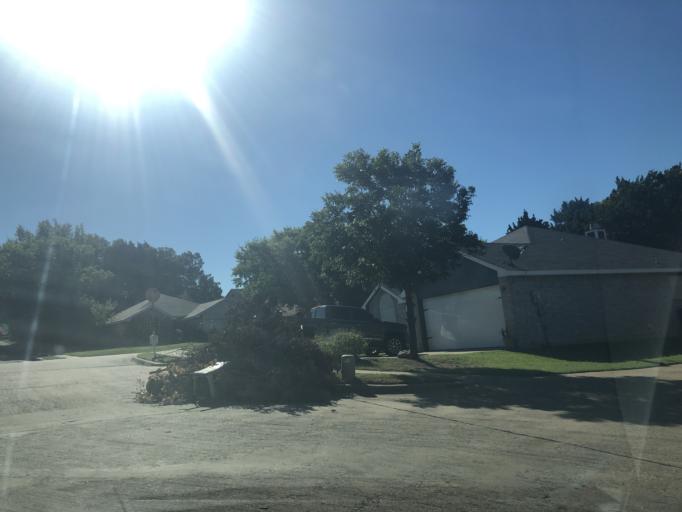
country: US
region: Texas
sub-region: Dallas County
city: Duncanville
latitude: 32.6655
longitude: -96.9363
